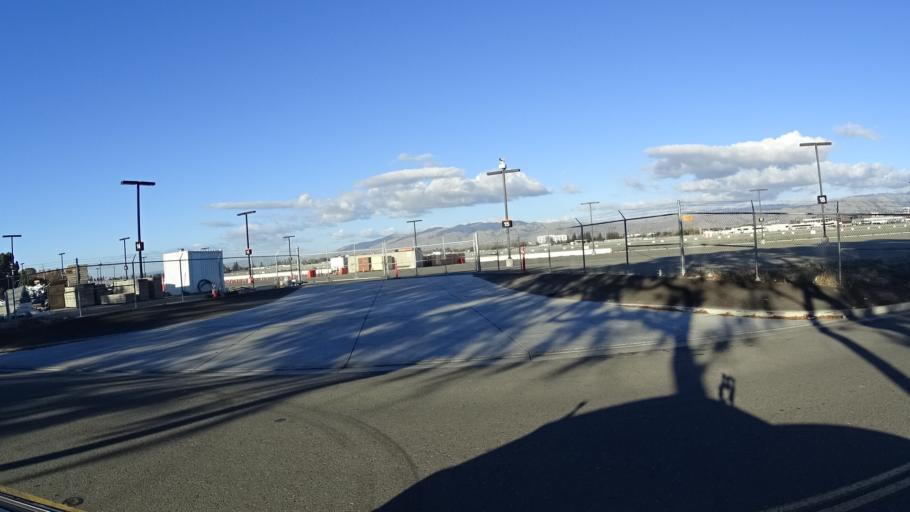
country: US
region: California
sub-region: Santa Clara County
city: Santa Clara
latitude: 37.3663
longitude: -121.9405
